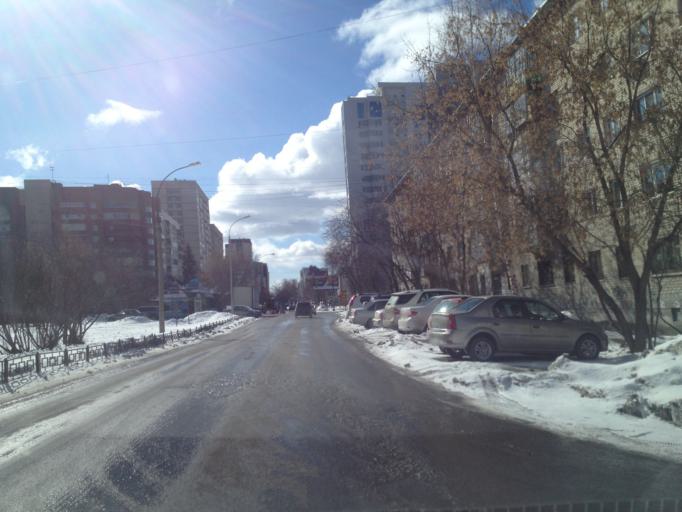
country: RU
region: Sverdlovsk
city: Yekaterinburg
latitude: 56.8158
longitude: 60.5961
